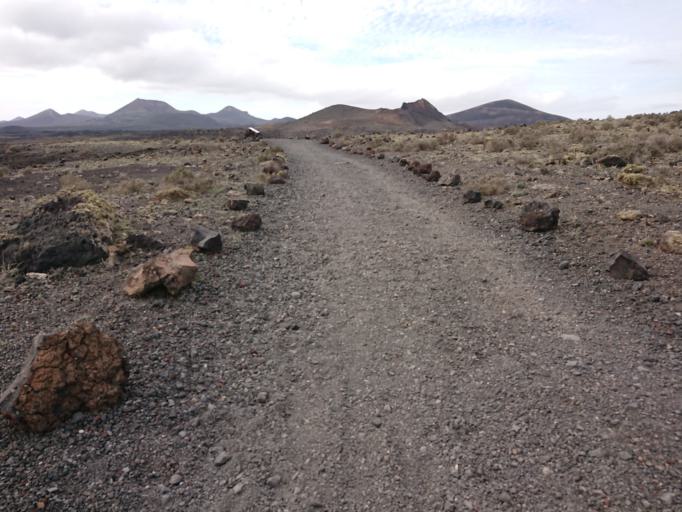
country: ES
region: Canary Islands
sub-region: Provincia de Las Palmas
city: Tias
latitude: 29.0029
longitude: -13.6808
